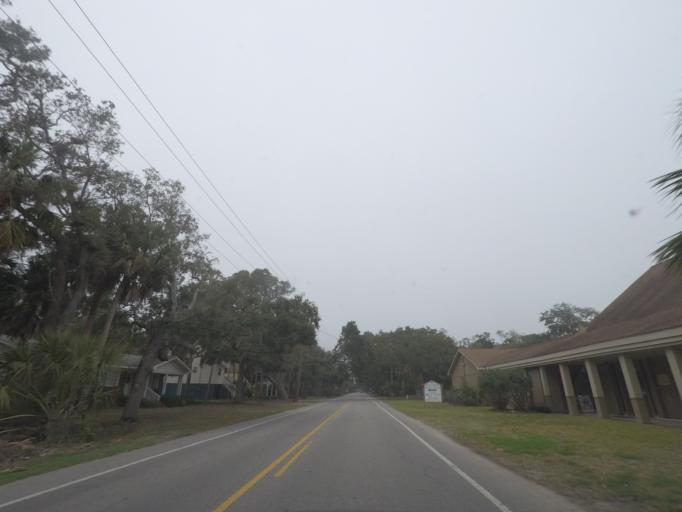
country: US
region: South Carolina
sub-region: Charleston County
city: Seabrook Island
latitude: 32.4976
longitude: -80.3095
